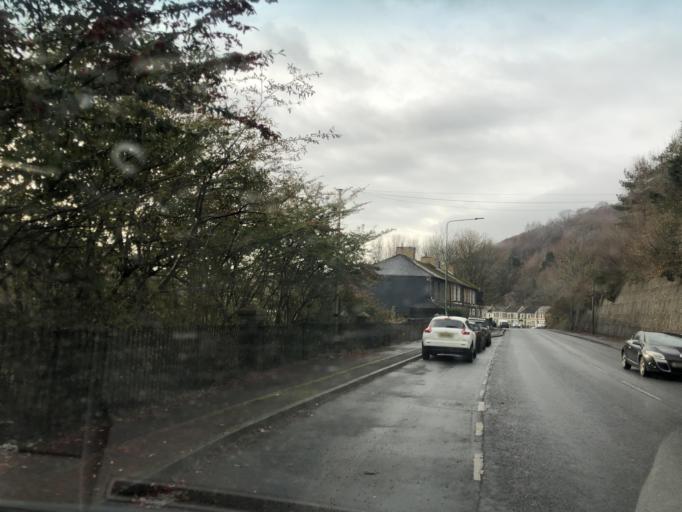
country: GB
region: Wales
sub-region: Blaenau Gwent
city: Abertillery
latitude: 51.7185
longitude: -3.1355
